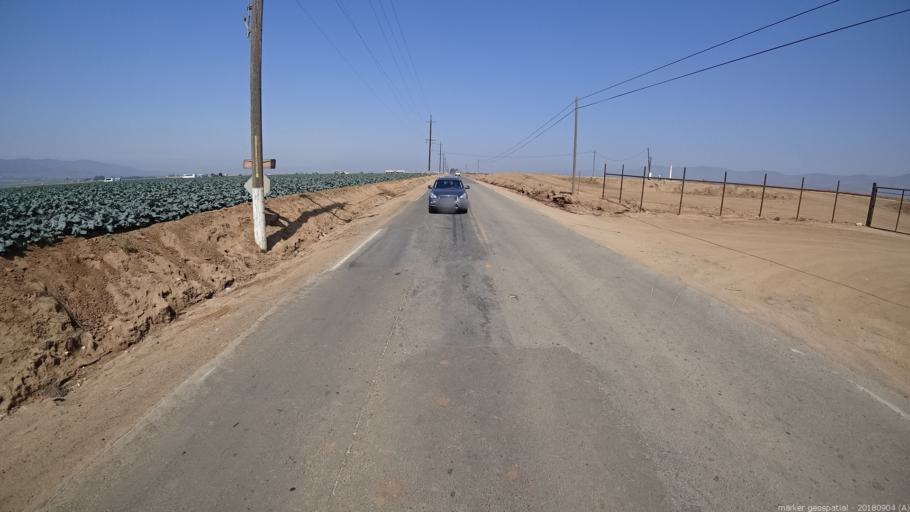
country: US
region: California
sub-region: Monterey County
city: Chualar
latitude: 36.5577
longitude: -121.4790
